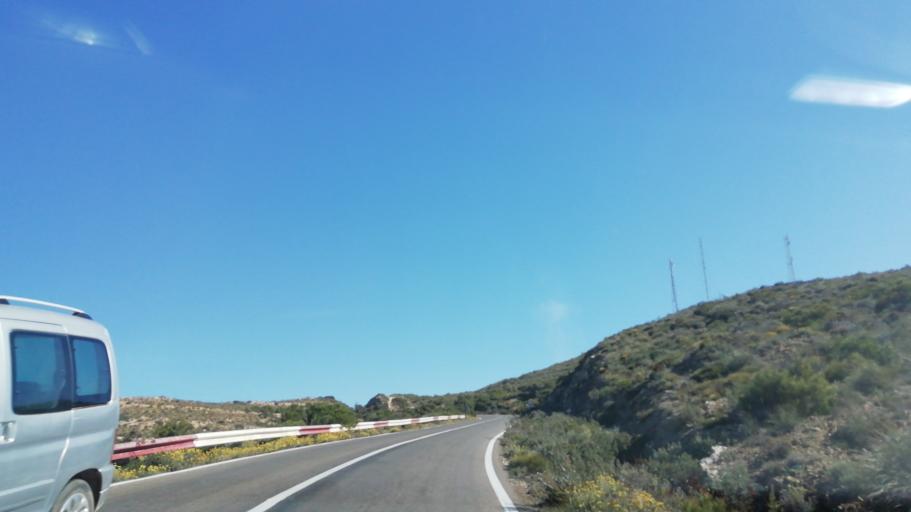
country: DZ
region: Ain Temouchent
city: El Amria
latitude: 35.6508
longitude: -1.0405
